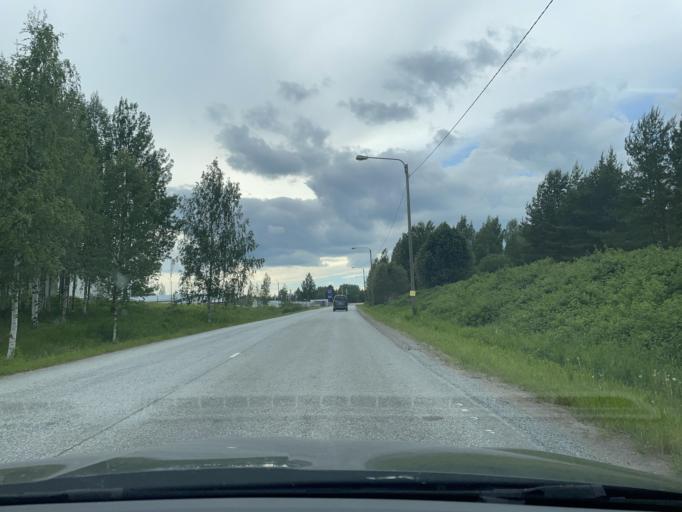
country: FI
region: Central Finland
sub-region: Jaemsae
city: Jaemsae
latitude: 61.8573
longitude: 25.1875
